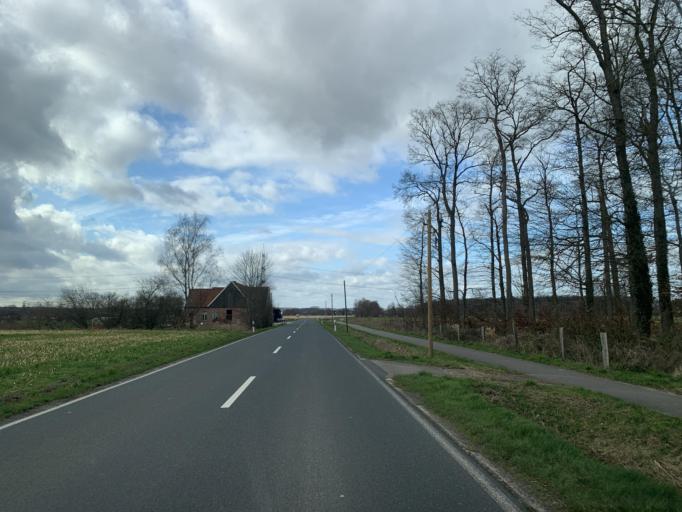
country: DE
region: North Rhine-Westphalia
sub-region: Regierungsbezirk Munster
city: Havixbeck
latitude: 52.0156
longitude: 7.4280
